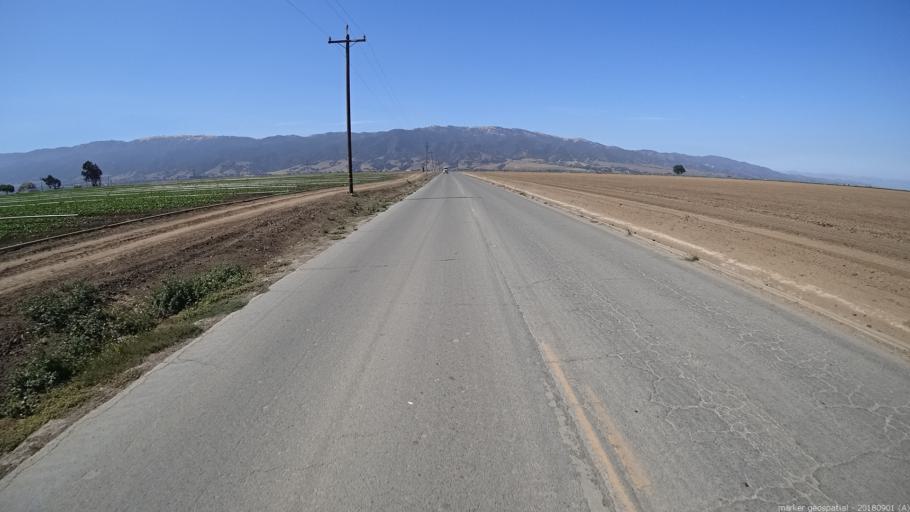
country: US
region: California
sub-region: Monterey County
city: Chualar
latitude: 36.5642
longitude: -121.5186
